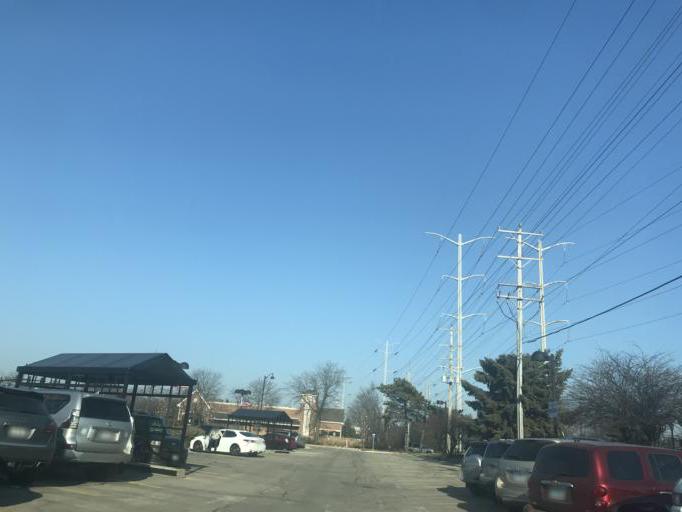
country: US
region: Illinois
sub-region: Cook County
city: Northfield
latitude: 42.1007
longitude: -87.7712
